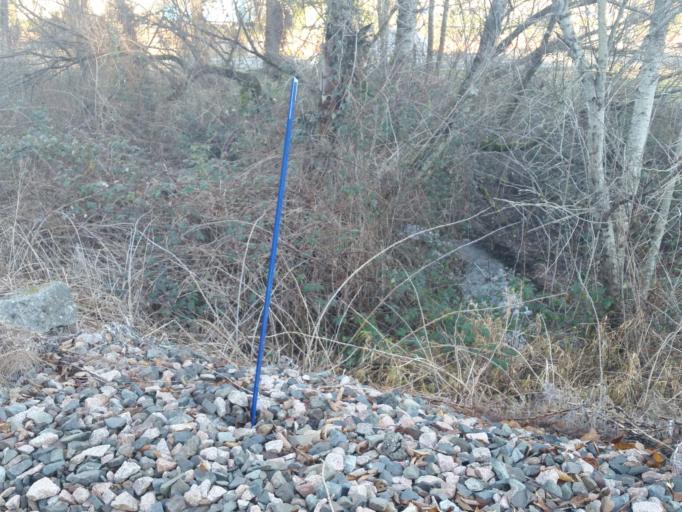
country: US
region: Washington
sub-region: King County
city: Woodinville
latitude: 47.7469
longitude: -122.1657
